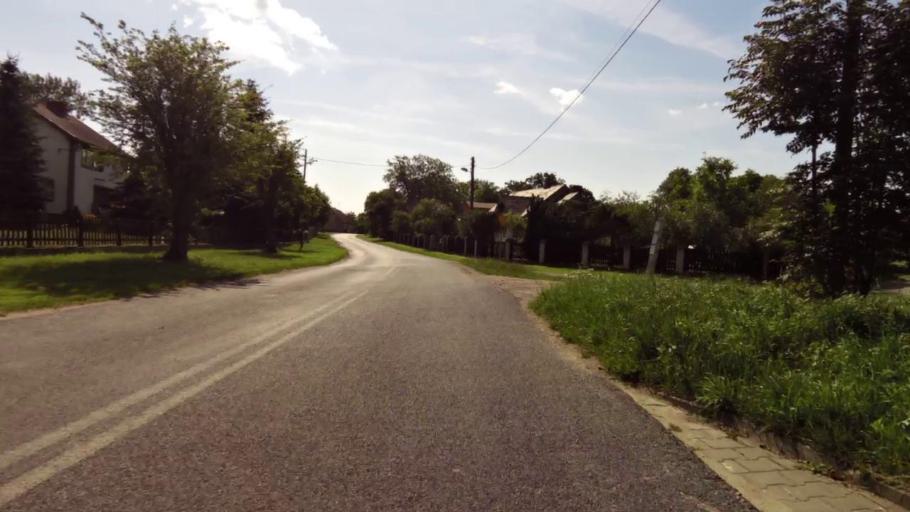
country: PL
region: West Pomeranian Voivodeship
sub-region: Powiat stargardzki
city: Dobrzany
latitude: 53.4114
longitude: 15.4235
